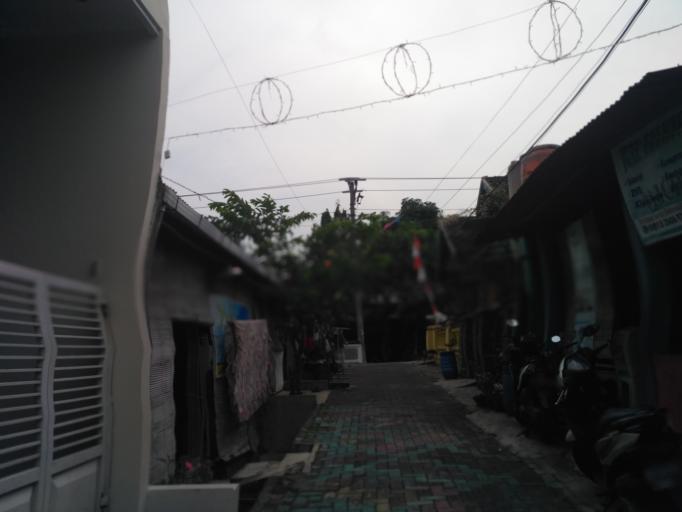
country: ID
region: Central Java
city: Ungaran
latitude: -7.0741
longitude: 110.4261
